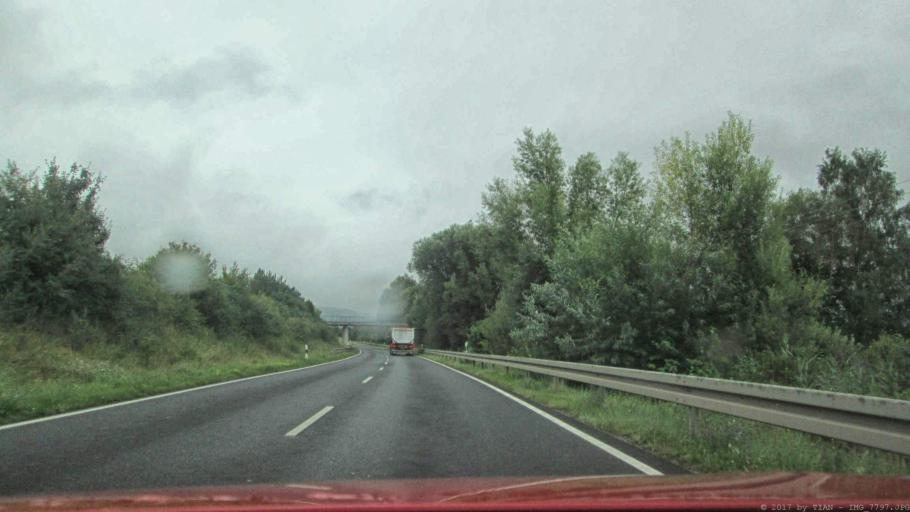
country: DE
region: Bavaria
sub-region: Regierungsbezirk Unterfranken
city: Zellingen
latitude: 49.8916
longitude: 9.8155
